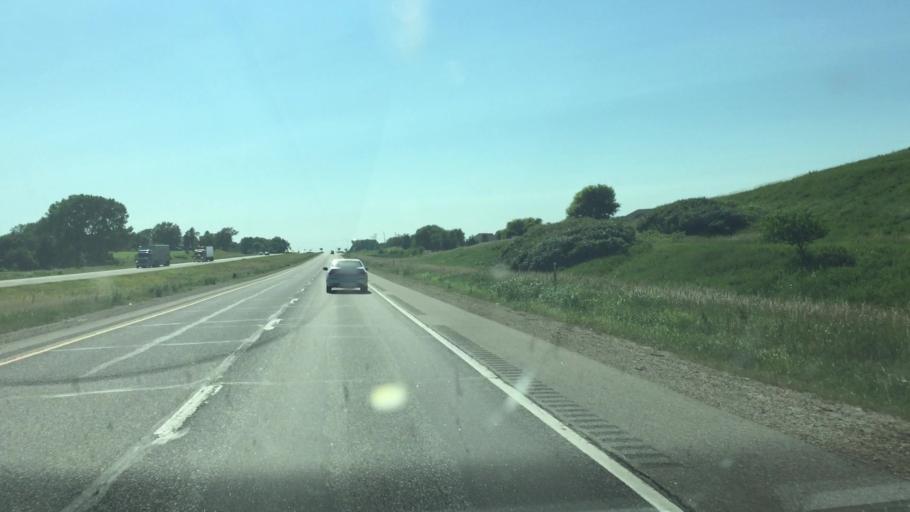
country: US
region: Iowa
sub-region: Linn County
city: Ely
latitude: 41.9264
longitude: -91.6100
